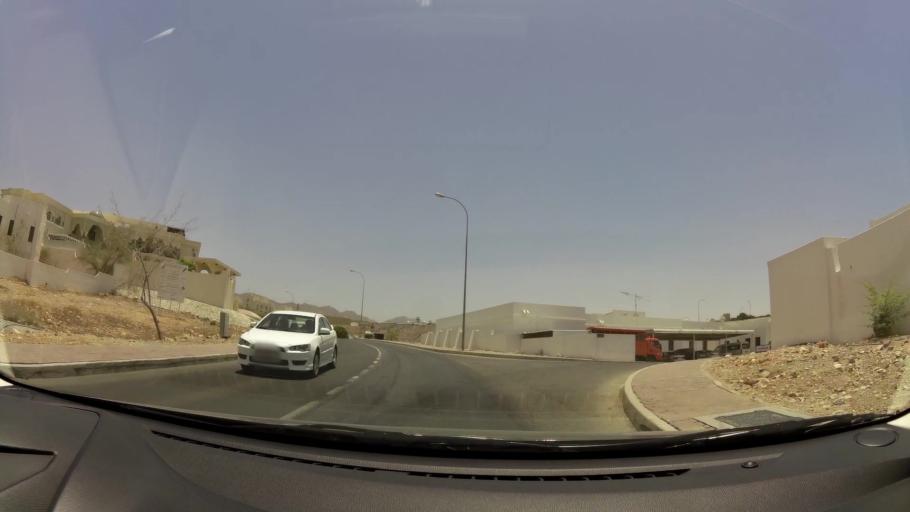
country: OM
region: Muhafazat Masqat
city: Bawshar
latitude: 23.6059
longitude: 58.4869
